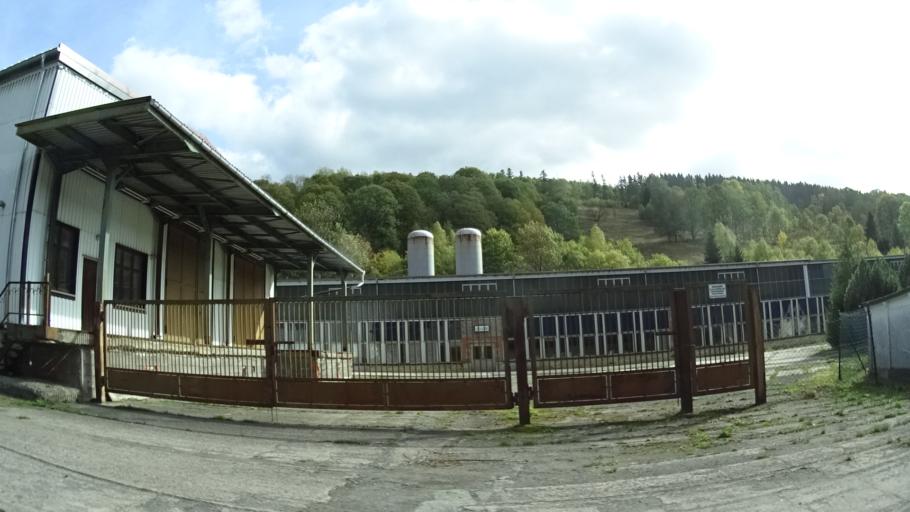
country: DE
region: Thuringia
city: Unterschonau
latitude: 50.7164
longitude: 10.5995
